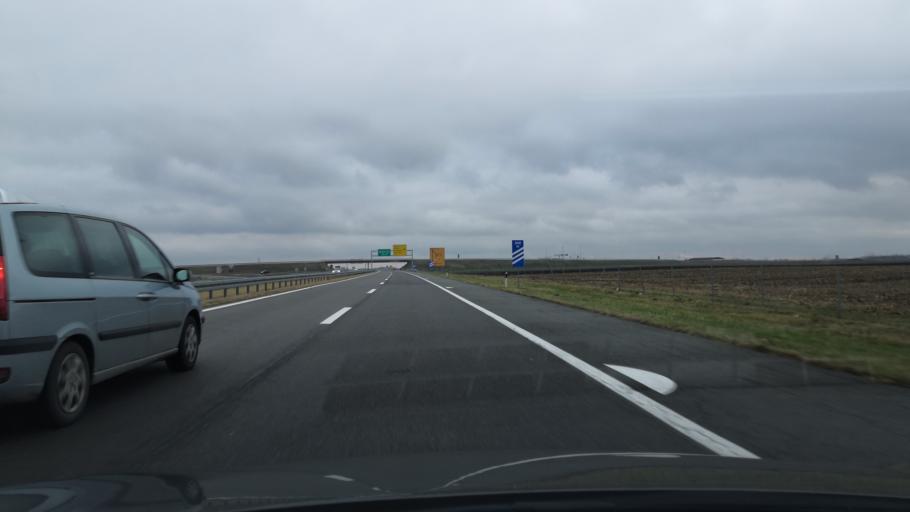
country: RS
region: Autonomna Pokrajina Vojvodina
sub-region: Severnobacki Okrug
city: Backa Topola
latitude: 45.8279
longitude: 19.6874
